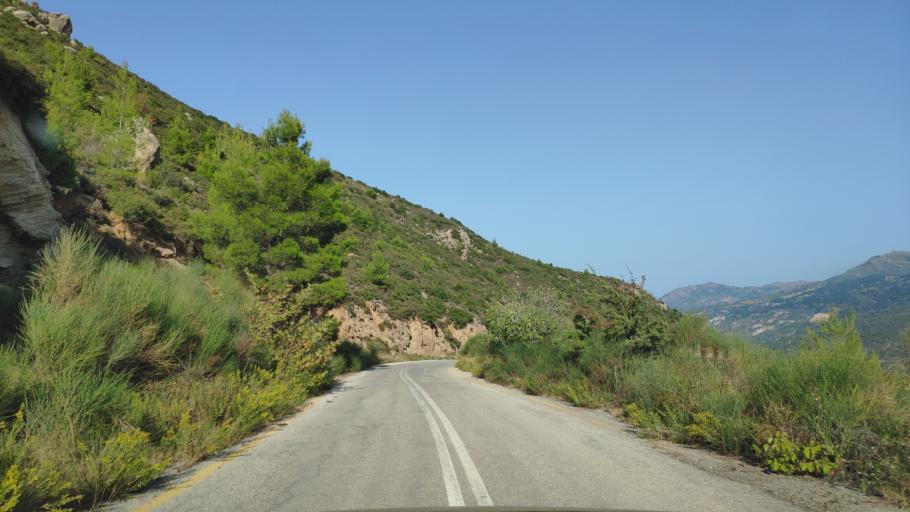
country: GR
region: West Greece
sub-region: Nomos Achaias
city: Aiyira
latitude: 38.0687
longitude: 22.3806
